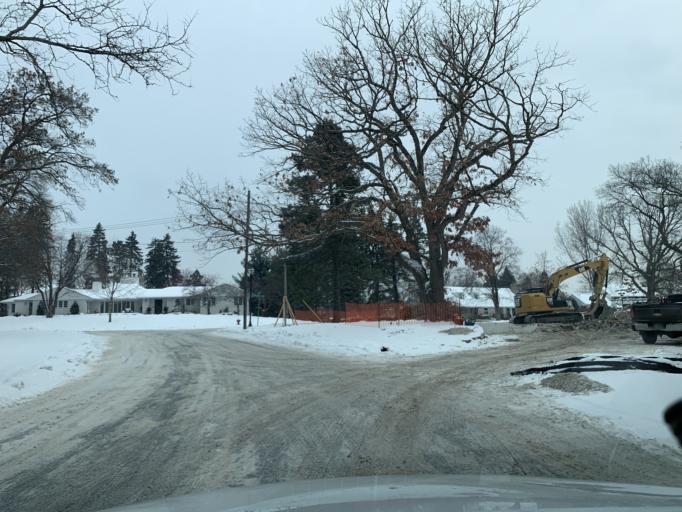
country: US
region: Minnesota
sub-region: Hennepin County
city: Edina
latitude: 44.9142
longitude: -93.3474
